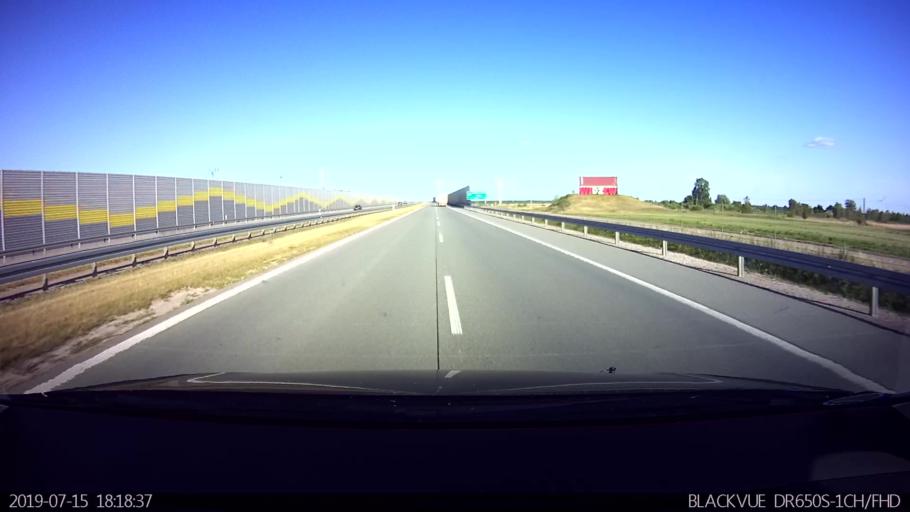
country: PL
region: Lodz Voivodeship
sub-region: Powiat laski
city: Sedziejowice
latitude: 51.5623
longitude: 18.9969
